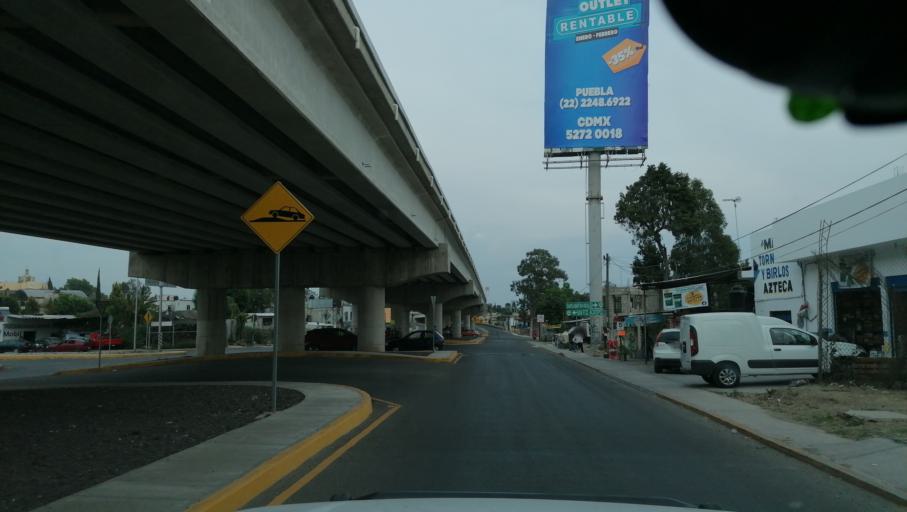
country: MX
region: Puebla
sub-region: San Gregorio Atzompa
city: Chipilo de Francisco Javier Mina
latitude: 19.0196
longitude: -98.3120
